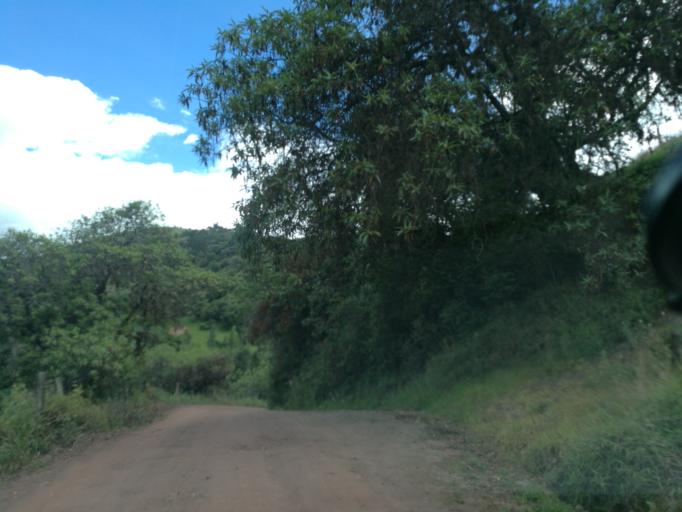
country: CO
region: Boyaca
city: Socota
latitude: 6.1149
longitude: -72.7172
